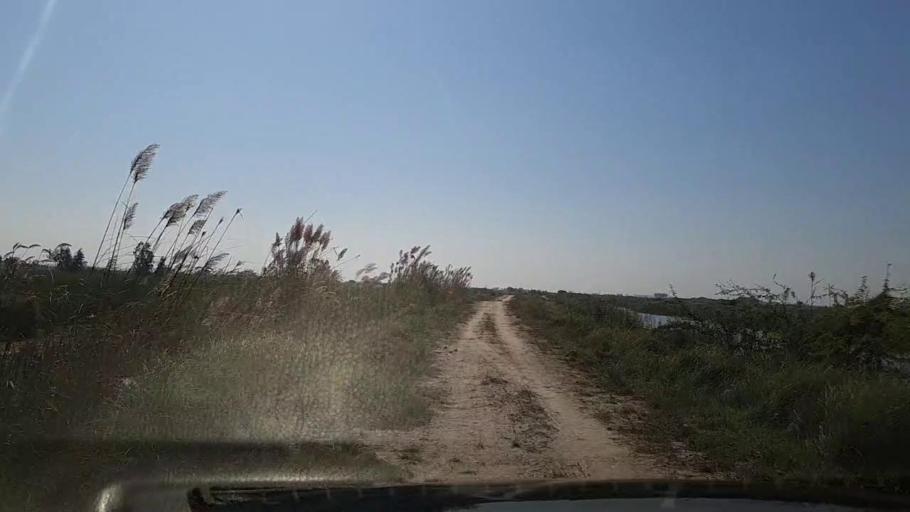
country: PK
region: Sindh
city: Thatta
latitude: 24.6718
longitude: 67.8890
